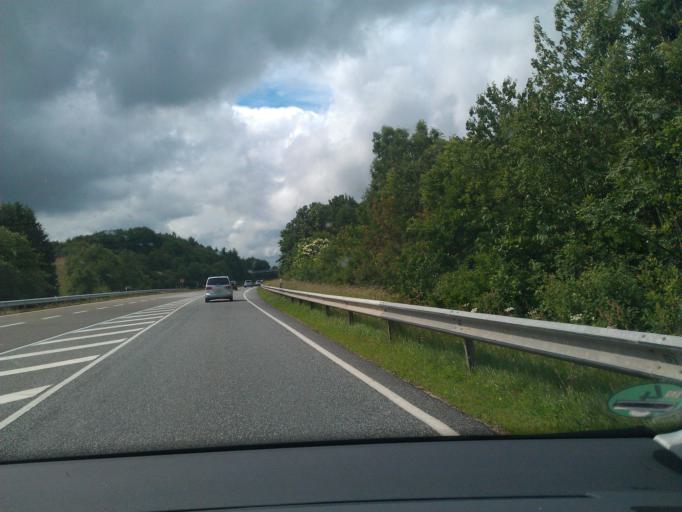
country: DE
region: Rheinland-Pfalz
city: Grosslangenfeld
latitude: 50.1999
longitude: 6.2579
